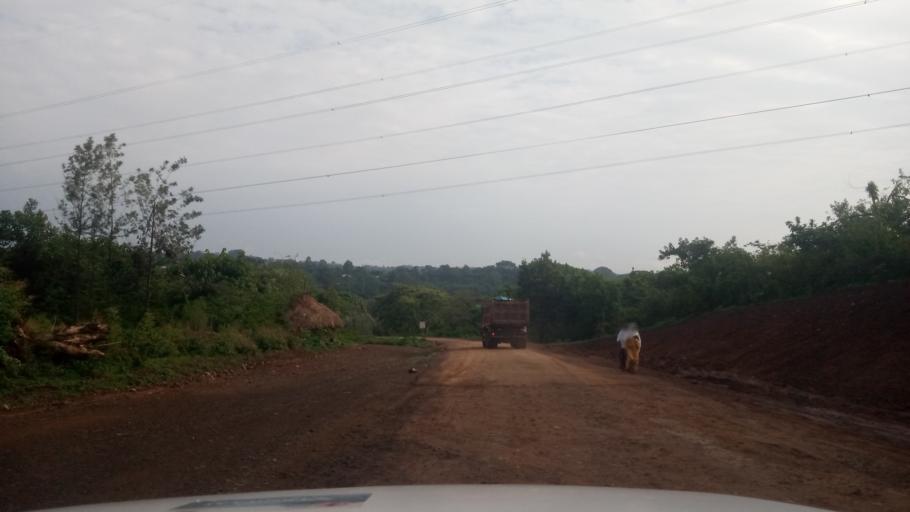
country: ET
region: Oromiya
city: Agaro
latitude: 7.8540
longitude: 36.6544
